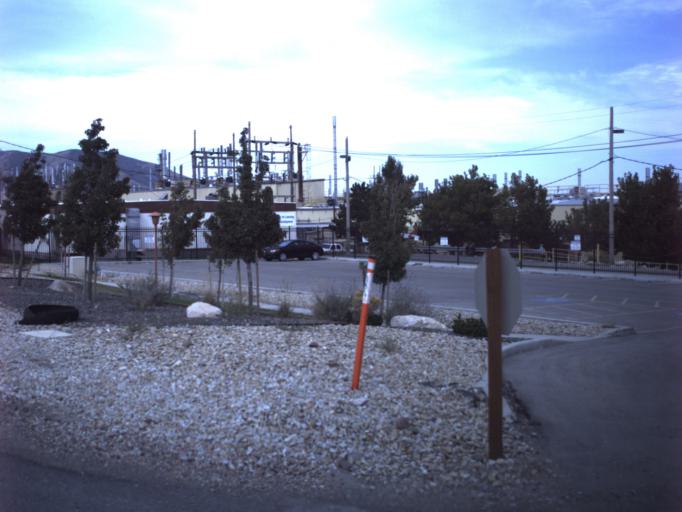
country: US
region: Utah
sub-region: Salt Lake County
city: Oquirrh
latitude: 40.6532
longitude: -112.0525
